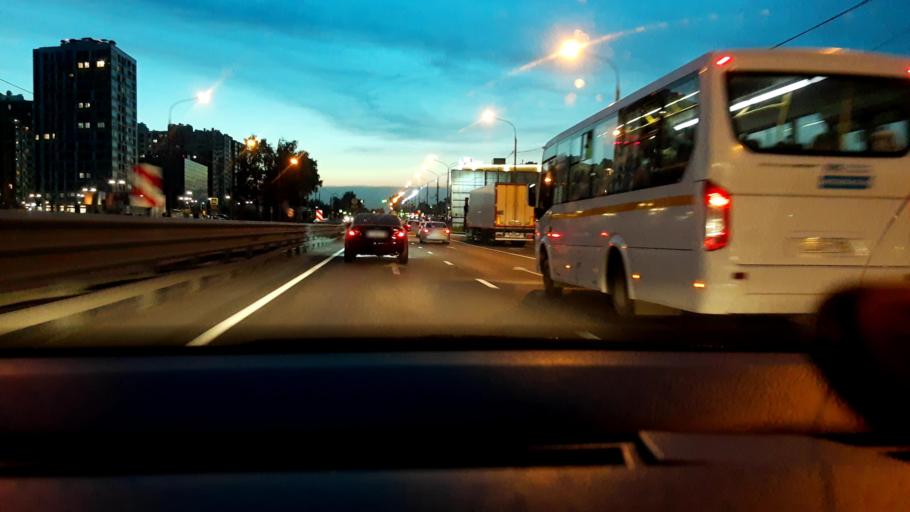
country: RU
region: Moscow
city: Vatutino
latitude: 55.9188
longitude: 37.6659
